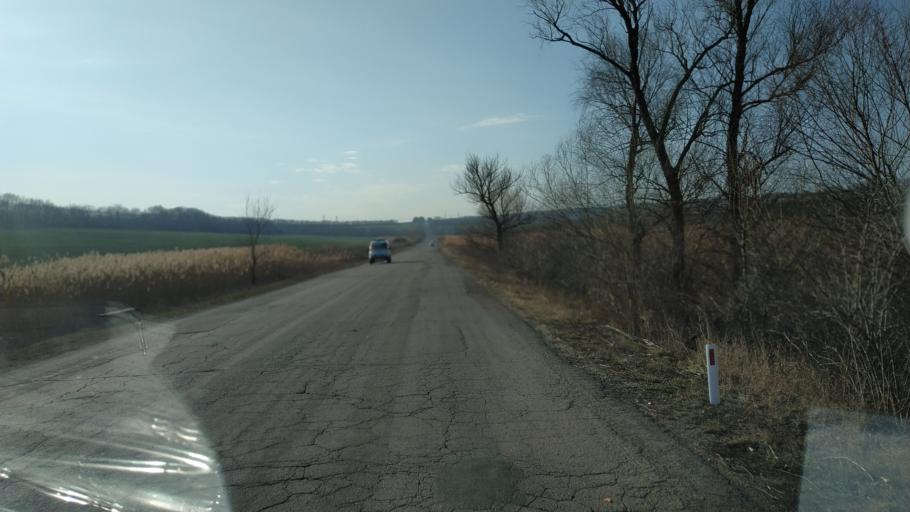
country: MD
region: Chisinau
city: Singera
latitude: 46.8866
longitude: 29.0392
